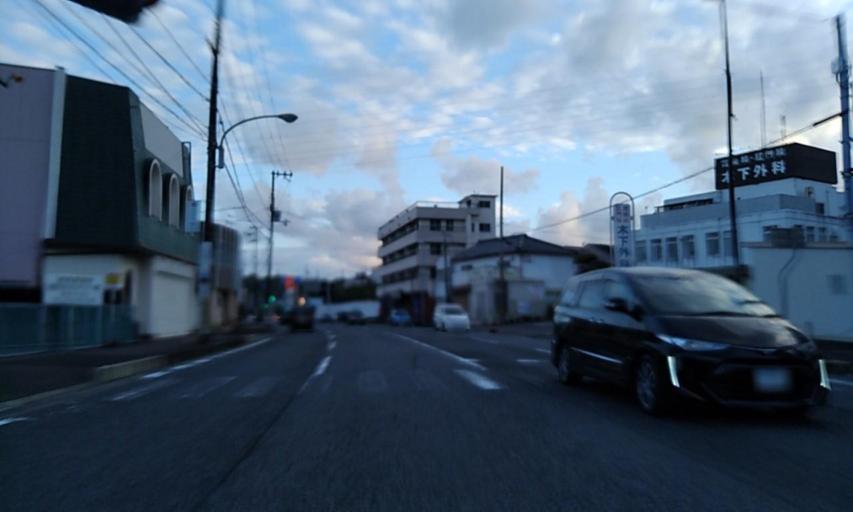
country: JP
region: Wakayama
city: Shingu
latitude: 33.7172
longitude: 135.9873
